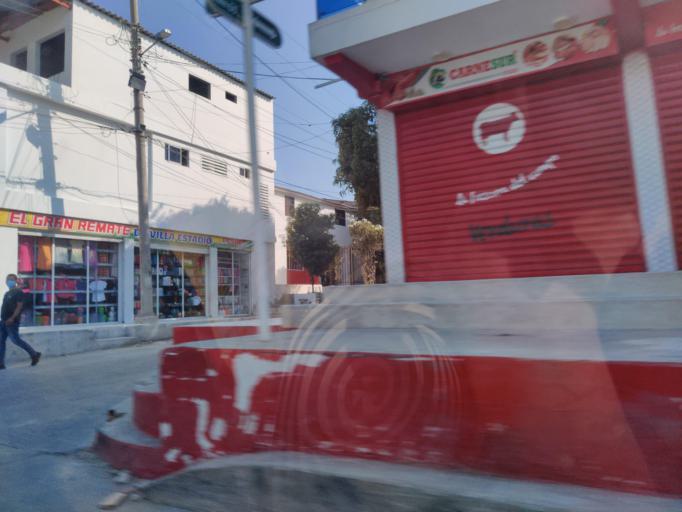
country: CO
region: Atlantico
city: Soledad
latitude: 10.9114
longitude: -74.8020
